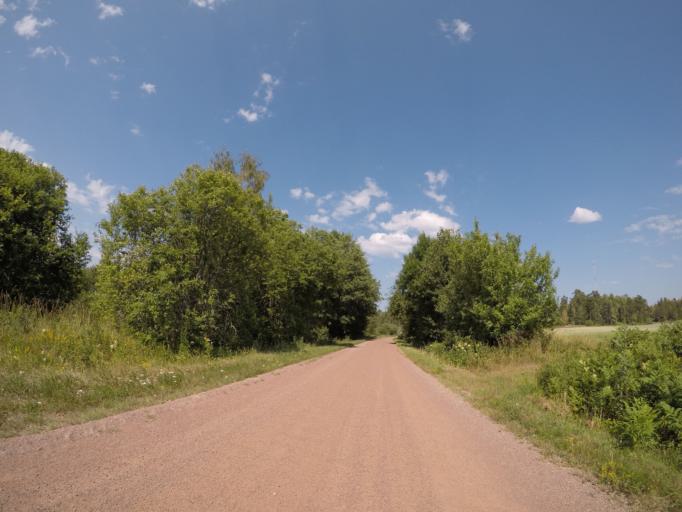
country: AX
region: Alands landsbygd
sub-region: Finstroem
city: Finstroem
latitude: 60.2159
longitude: 19.8556
